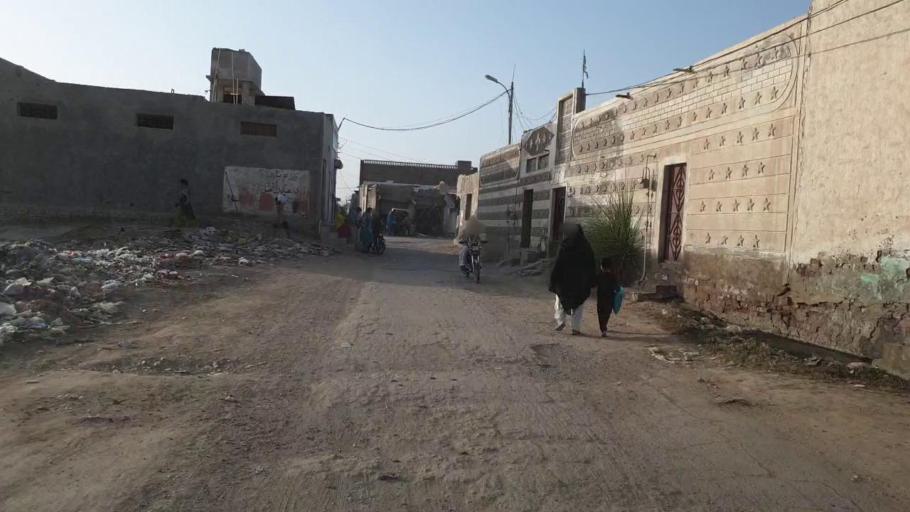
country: PK
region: Sindh
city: Jam Sahib
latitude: 26.2946
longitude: 68.6268
